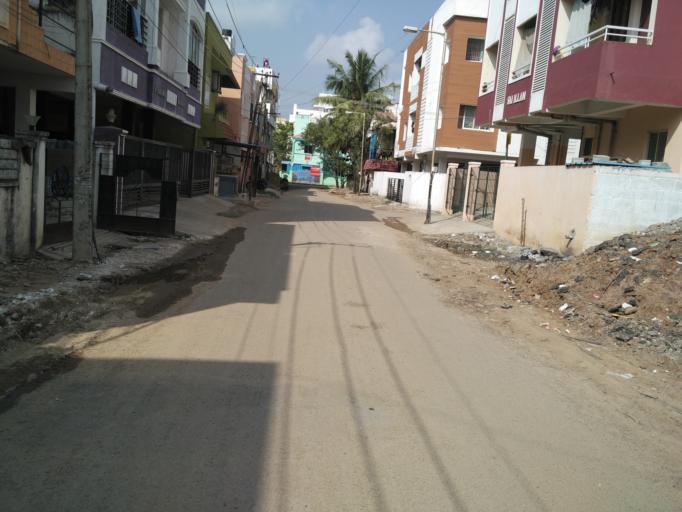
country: IN
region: Tamil Nadu
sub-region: Kancheepuram
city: Perungudi
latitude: 12.9516
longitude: 80.2357
